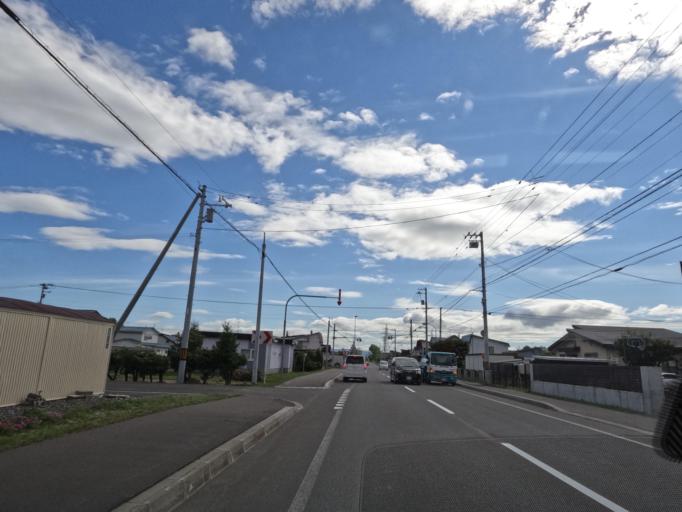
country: JP
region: Hokkaido
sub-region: Asahikawa-shi
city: Asahikawa
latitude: 43.8263
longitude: 142.5225
